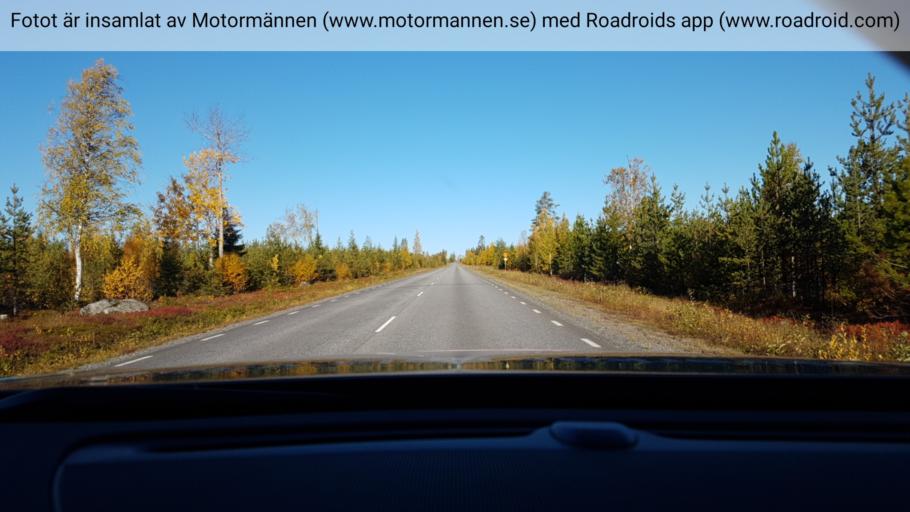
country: SE
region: Vaesterbotten
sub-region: Skelleftea Kommun
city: Storvik
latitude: 65.3438
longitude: 20.5147
